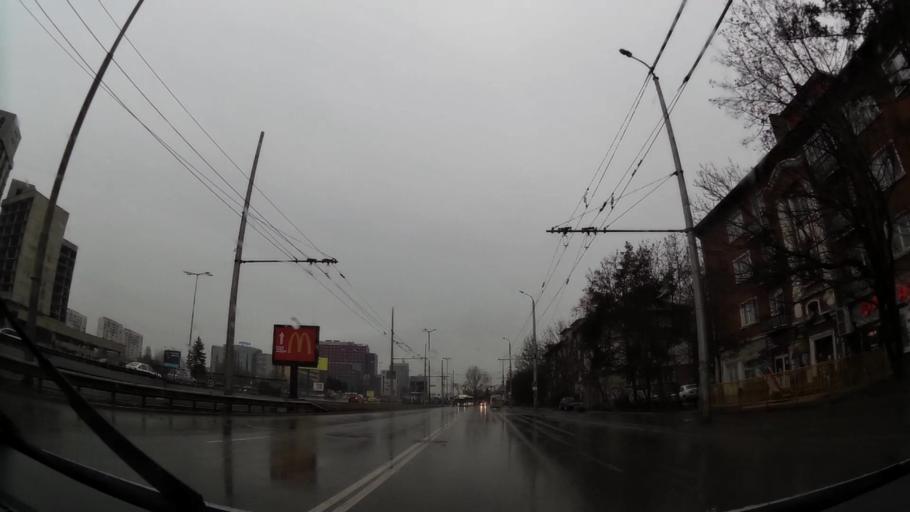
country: BG
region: Sofia-Capital
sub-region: Stolichna Obshtina
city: Sofia
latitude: 42.6636
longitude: 23.3748
